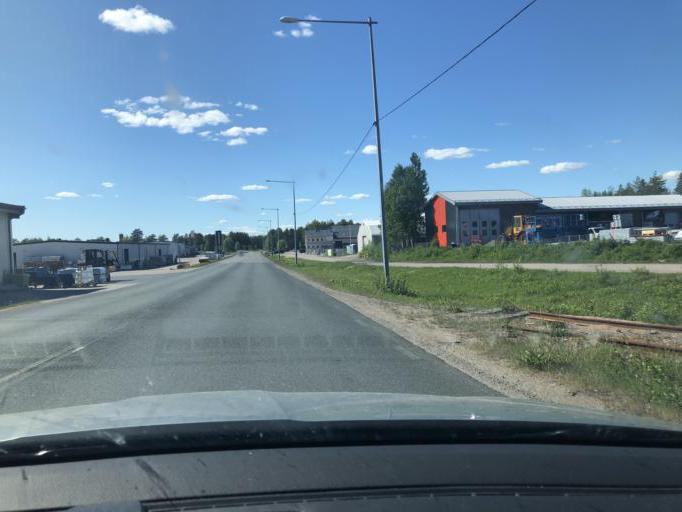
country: SE
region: Norrbotten
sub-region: Kalix Kommun
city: Kalix
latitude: 65.8621
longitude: 23.1467
